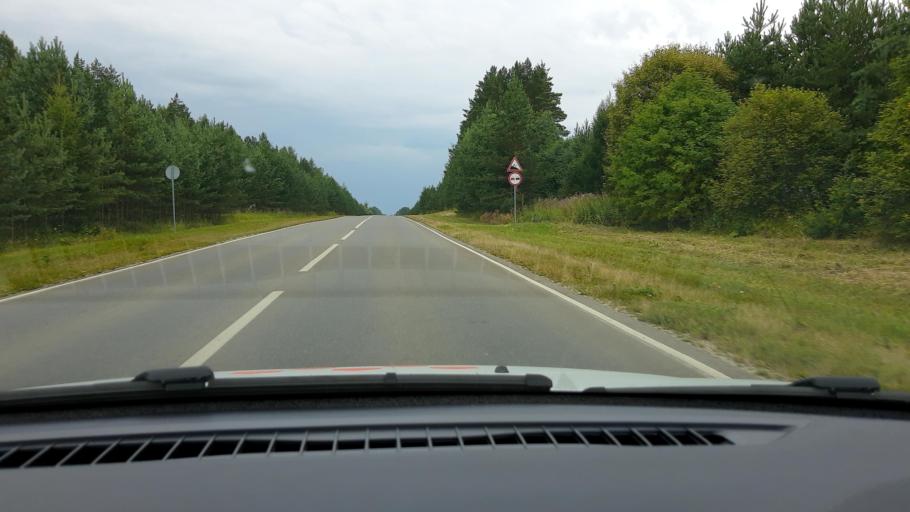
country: RU
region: Nizjnij Novgorod
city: Sarov
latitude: 55.1404
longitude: 43.5600
